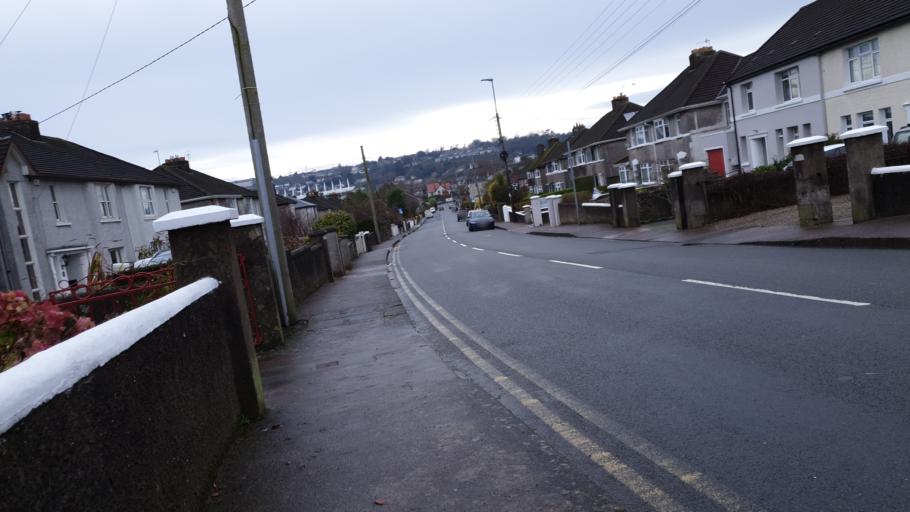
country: IE
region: Munster
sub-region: County Cork
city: Cork
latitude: 51.8933
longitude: -8.4302
